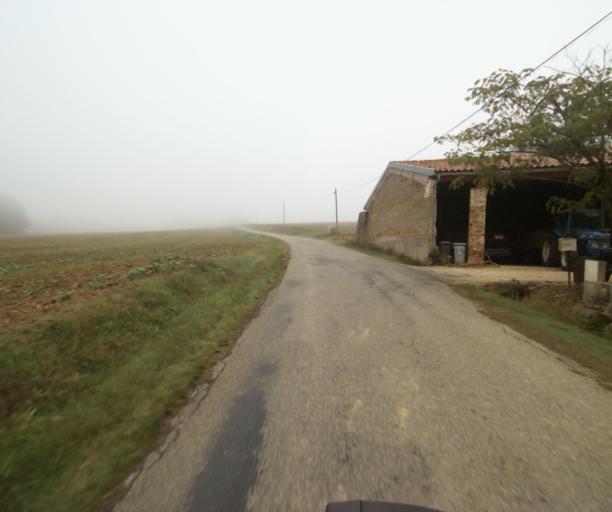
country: FR
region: Midi-Pyrenees
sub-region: Departement du Tarn-et-Garonne
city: Nohic
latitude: 43.9326
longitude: 1.4802
